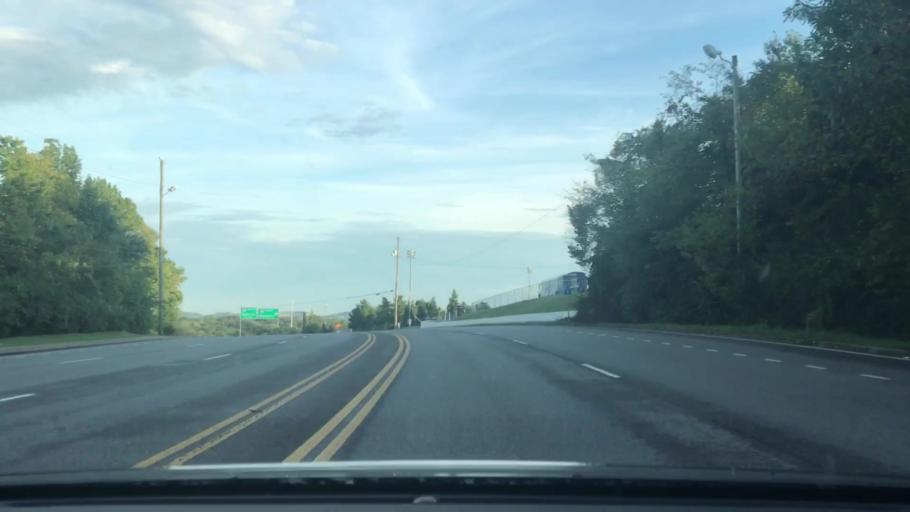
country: US
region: Tennessee
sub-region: Davidson County
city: Oak Hill
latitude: 36.0843
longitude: -86.7679
